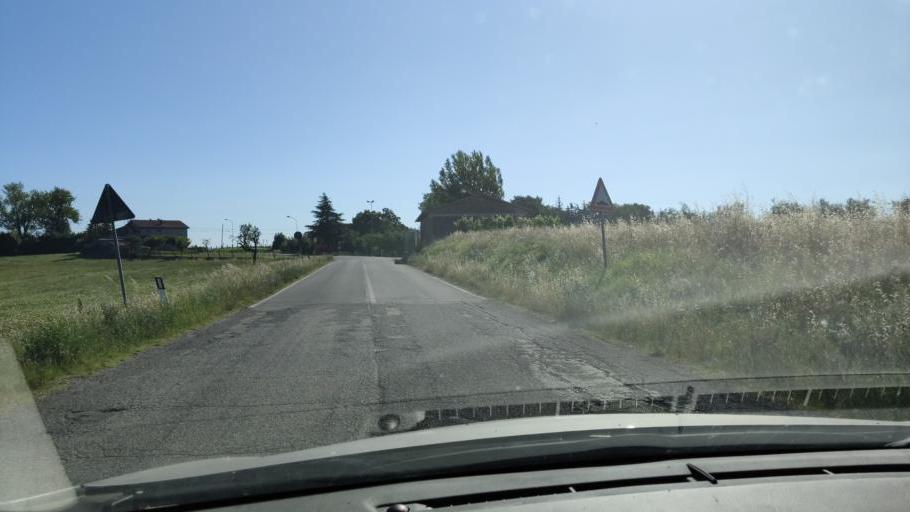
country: IT
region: Umbria
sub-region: Provincia di Terni
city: Avigliano Umbro
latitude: 42.6600
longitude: 12.4366
